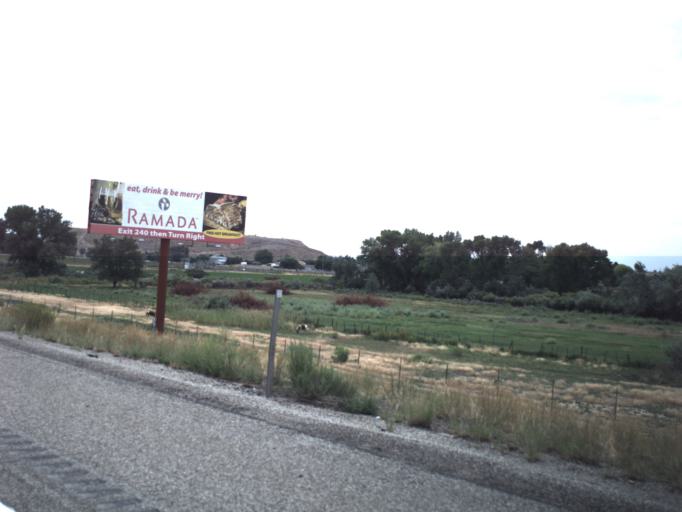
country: US
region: Utah
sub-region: Carbon County
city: Carbonville
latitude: 39.6160
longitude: -110.8490
